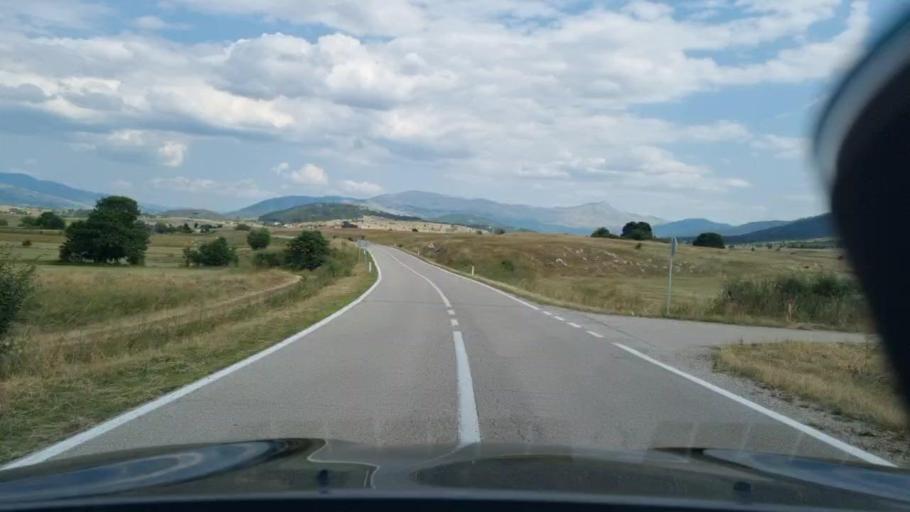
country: BA
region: Federation of Bosnia and Herzegovina
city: Bosansko Grahovo
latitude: 44.1637
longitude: 16.3798
